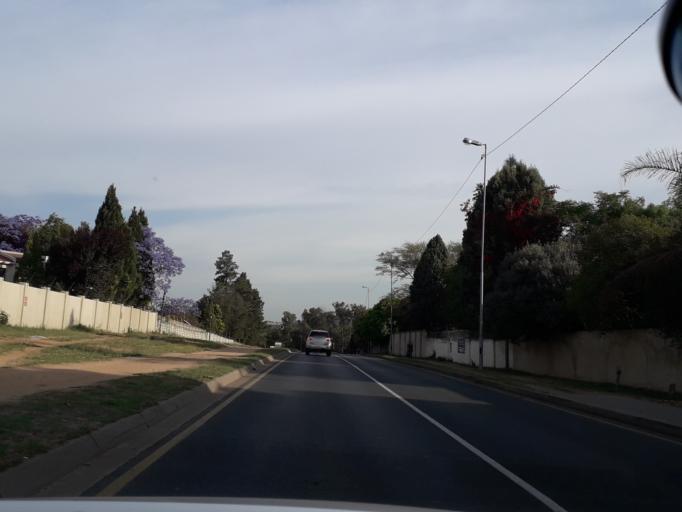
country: ZA
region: Gauteng
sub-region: City of Johannesburg Metropolitan Municipality
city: Diepsloot
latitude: -26.0416
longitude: 27.9956
